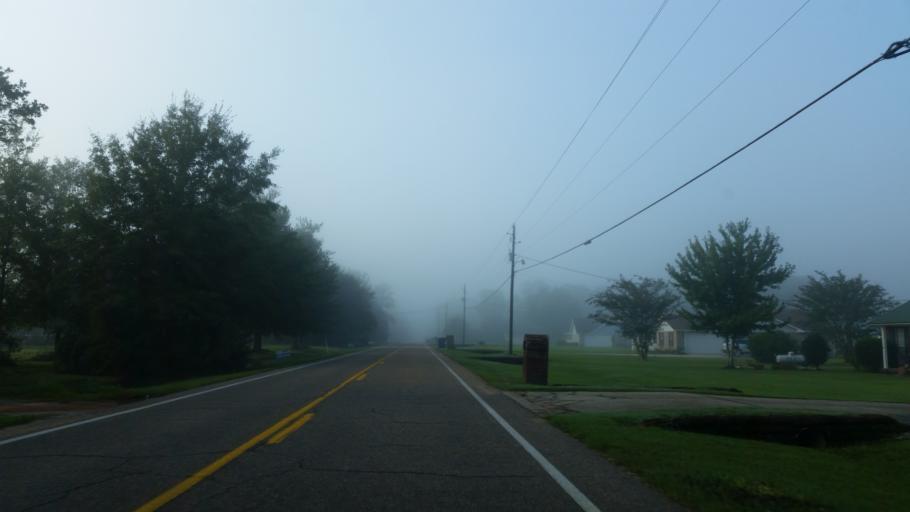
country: US
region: Florida
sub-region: Escambia County
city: Molino
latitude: 30.7296
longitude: -87.3440
